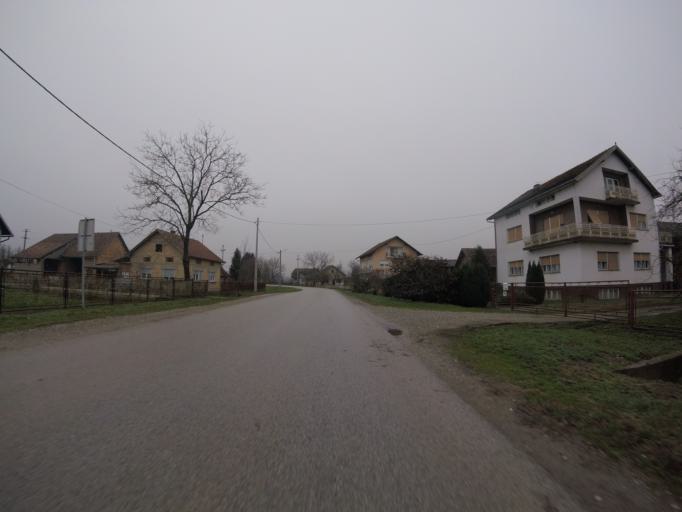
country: HR
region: Sisacko-Moslavacka
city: Lekenik
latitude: 45.6210
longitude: 16.3260
